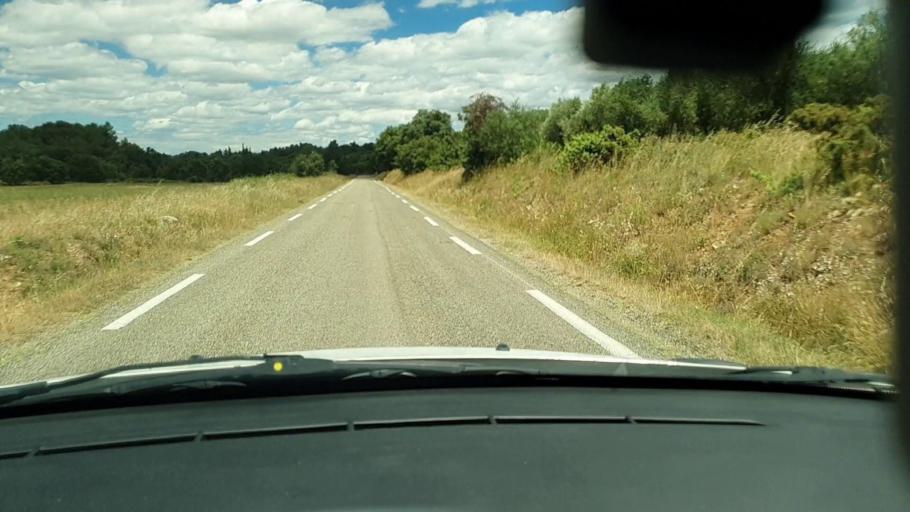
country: FR
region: Languedoc-Roussillon
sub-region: Departement du Gard
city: Cabrieres
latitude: 43.9203
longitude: 4.4736
